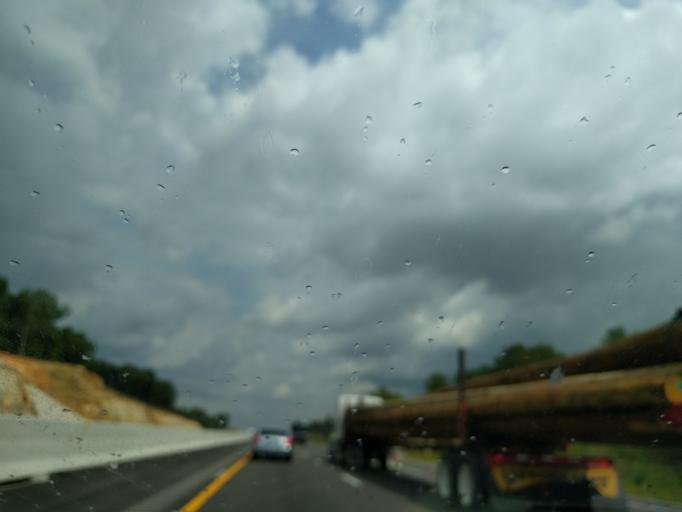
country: US
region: Kentucky
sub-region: Hart County
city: Munfordville
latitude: 37.4171
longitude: -85.8820
